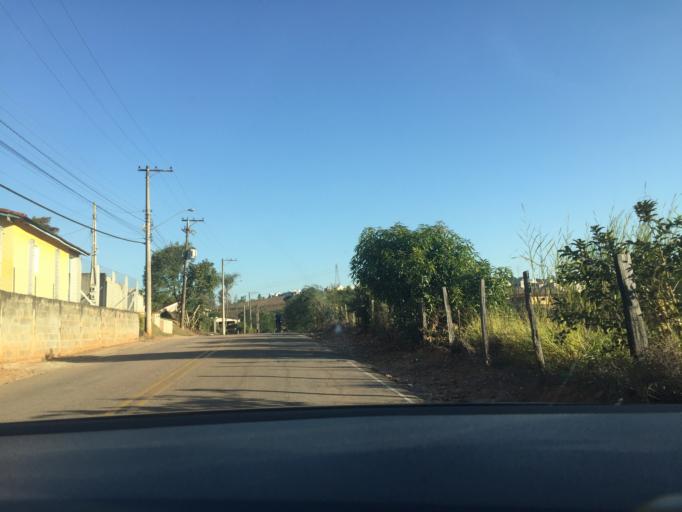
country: BR
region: Sao Paulo
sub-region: Louveira
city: Louveira
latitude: -23.1151
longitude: -46.9168
